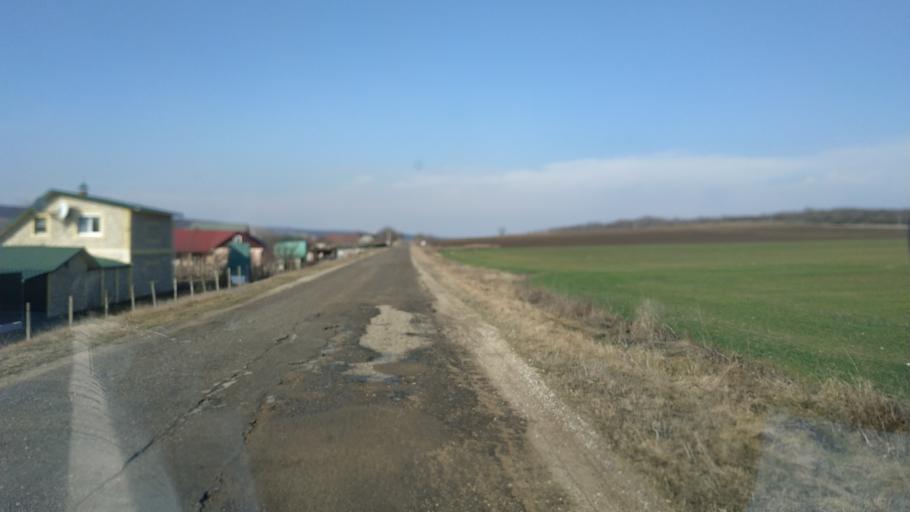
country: MD
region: Chisinau
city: Singera
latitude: 46.6879
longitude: 29.0496
